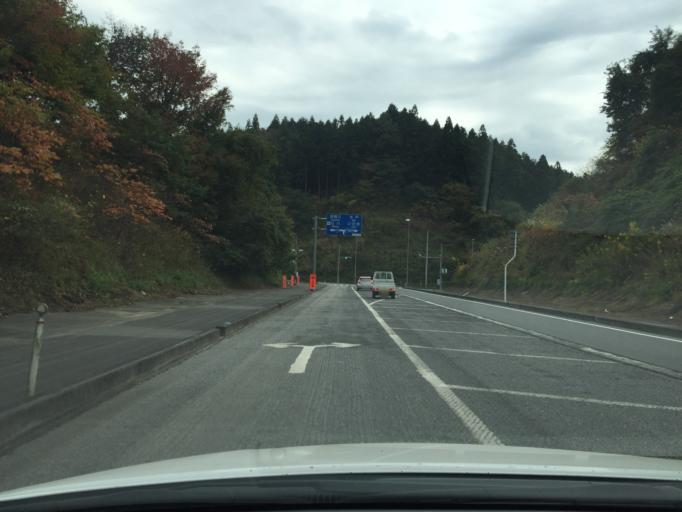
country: JP
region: Fukushima
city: Ishikawa
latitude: 37.0442
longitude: 140.3749
